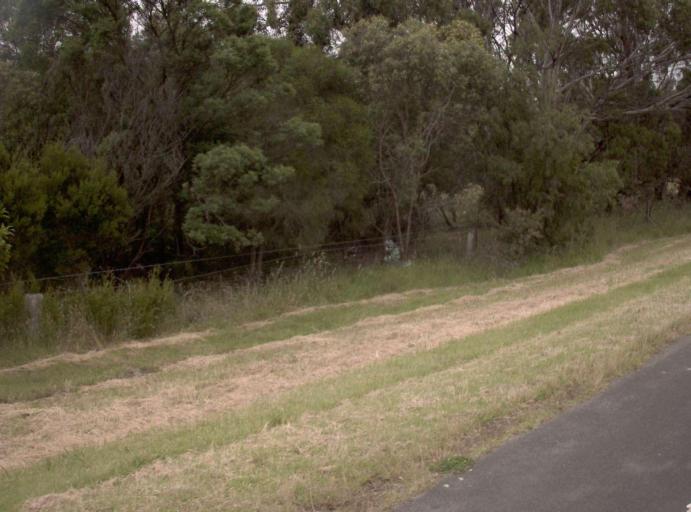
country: AU
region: Victoria
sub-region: Latrobe
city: Morwell
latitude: -38.2704
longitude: 146.4233
